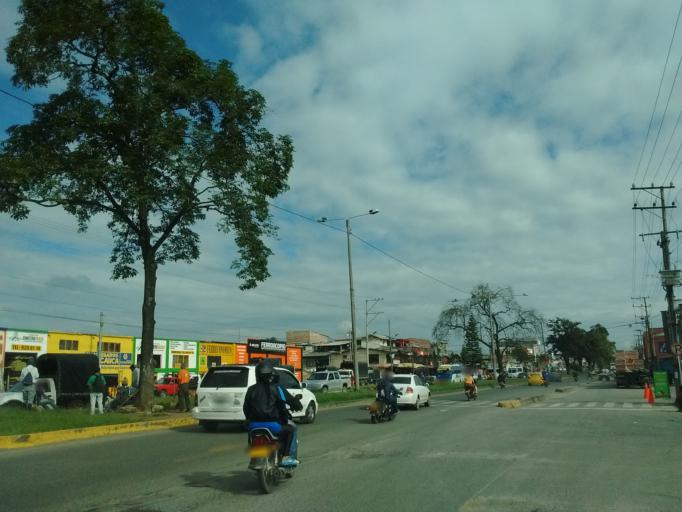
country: CO
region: Cauca
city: Popayan
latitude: 2.4372
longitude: -76.6161
